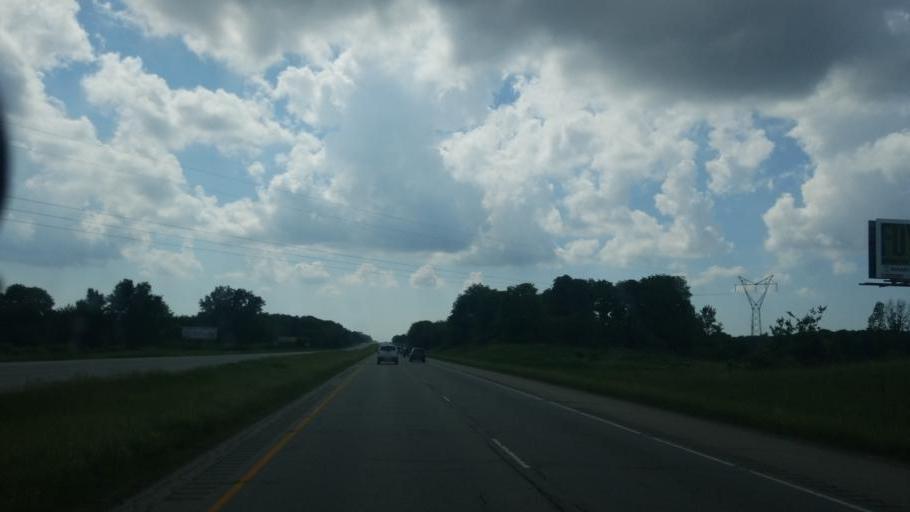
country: US
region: Indiana
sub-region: Kosciusko County
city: Warsaw
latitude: 41.2700
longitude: -85.8840
